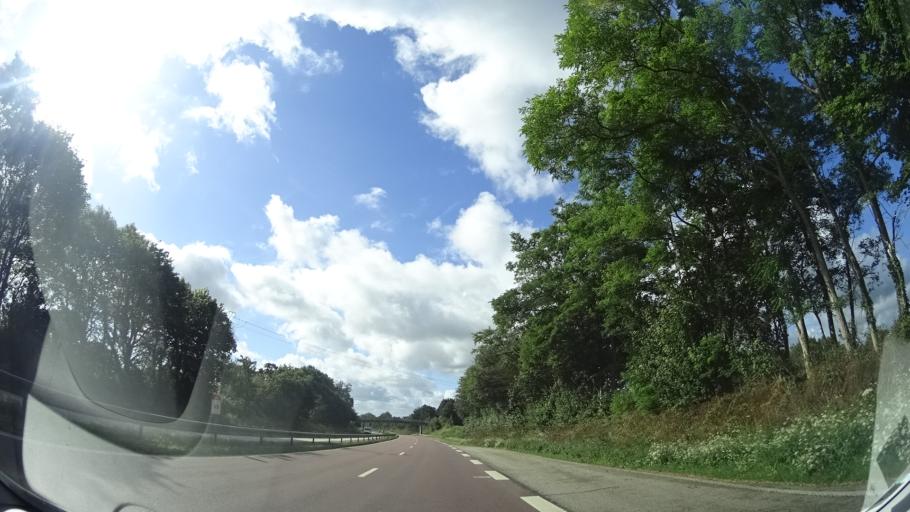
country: FR
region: Lower Normandy
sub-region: Departement de la Manche
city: Valognes
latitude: 49.5066
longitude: -1.4928
